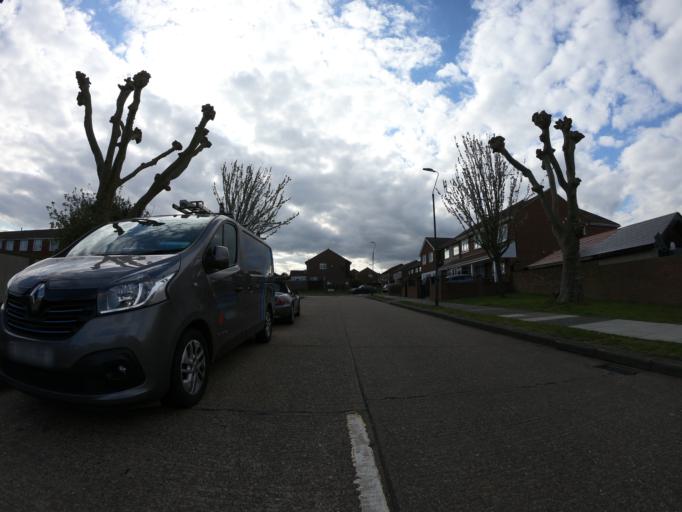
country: GB
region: England
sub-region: Greater London
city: Belvedere
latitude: 51.4824
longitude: 0.1400
